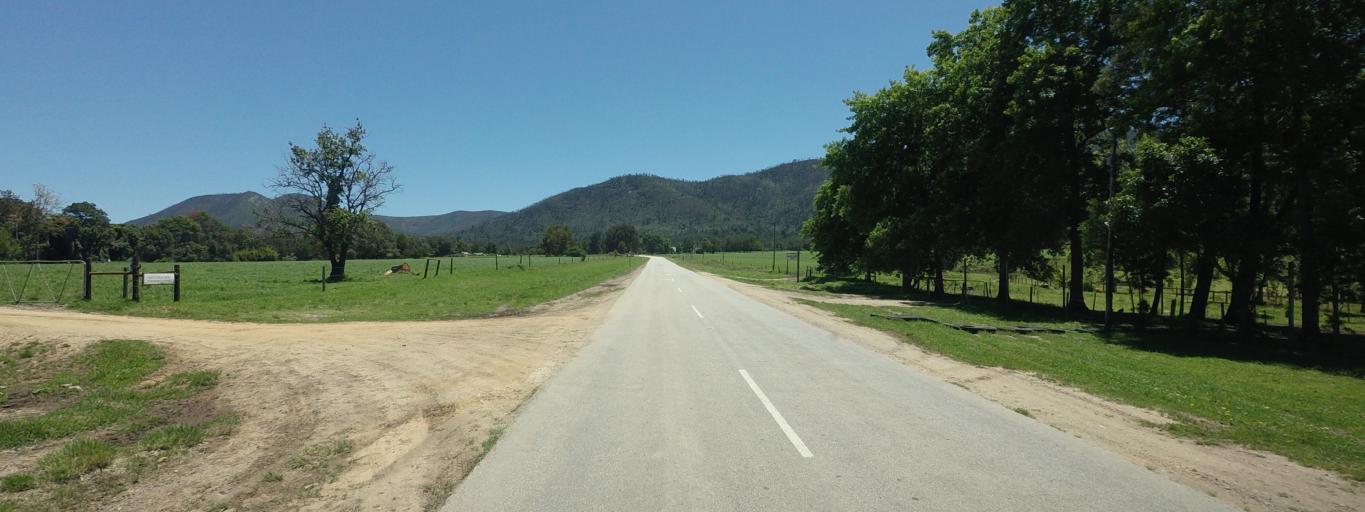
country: ZA
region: Western Cape
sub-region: Eden District Municipality
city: Plettenberg Bay
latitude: -33.9419
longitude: 23.5110
